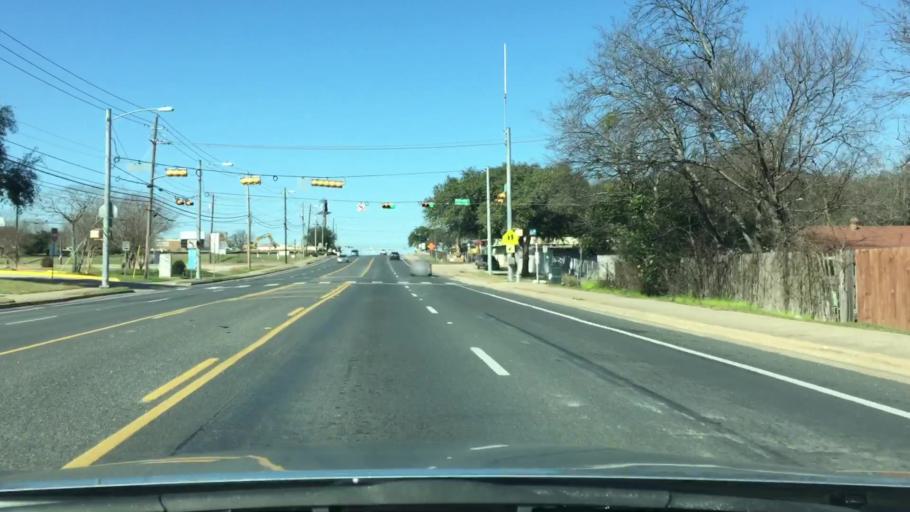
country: US
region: Texas
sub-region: Travis County
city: Wells Branch
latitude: 30.3799
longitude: -97.6830
